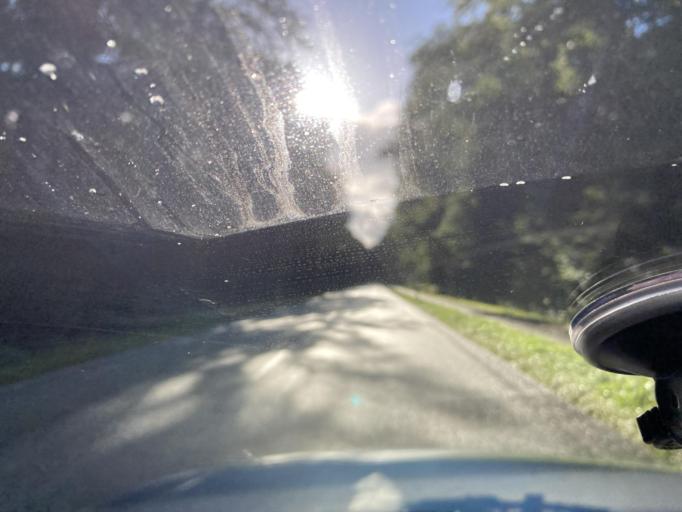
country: DE
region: Schleswig-Holstein
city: Elsdorf-Westermuhlen
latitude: 54.2658
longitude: 9.5498
